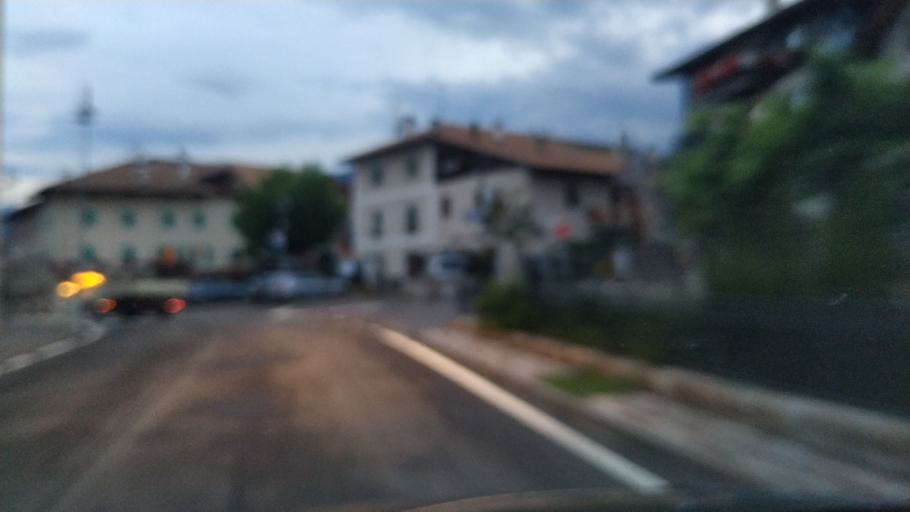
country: IT
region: Trentino-Alto Adige
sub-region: Provincia di Trento
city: Romallo
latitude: 46.3967
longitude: 11.0665
